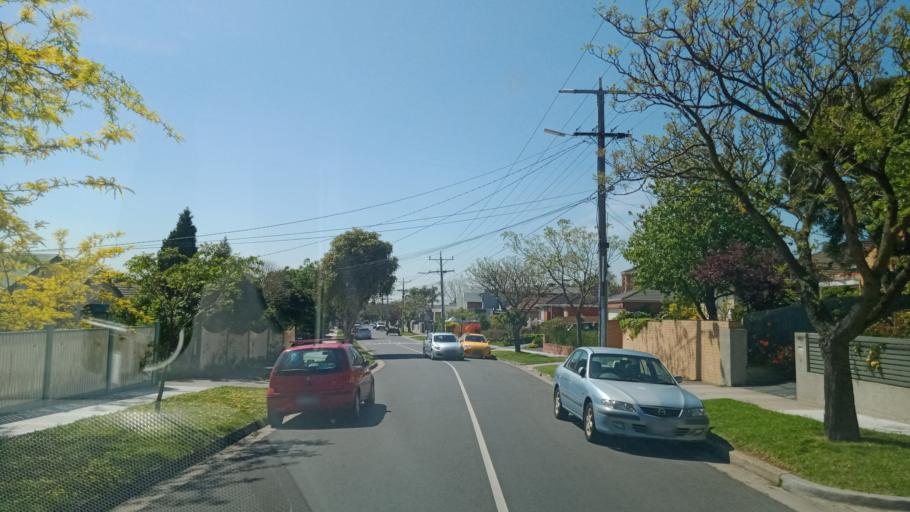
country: AU
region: Victoria
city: Murrumbeena
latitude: -37.9141
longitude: 145.0652
